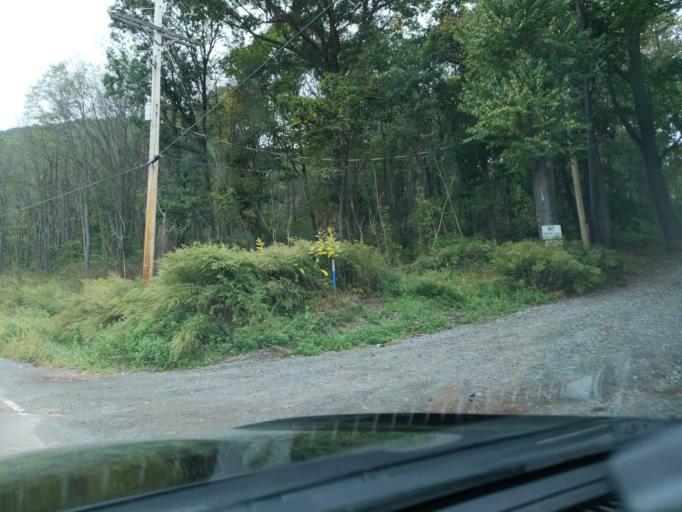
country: US
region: Pennsylvania
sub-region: Blair County
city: Altoona
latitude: 40.4979
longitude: -78.4696
